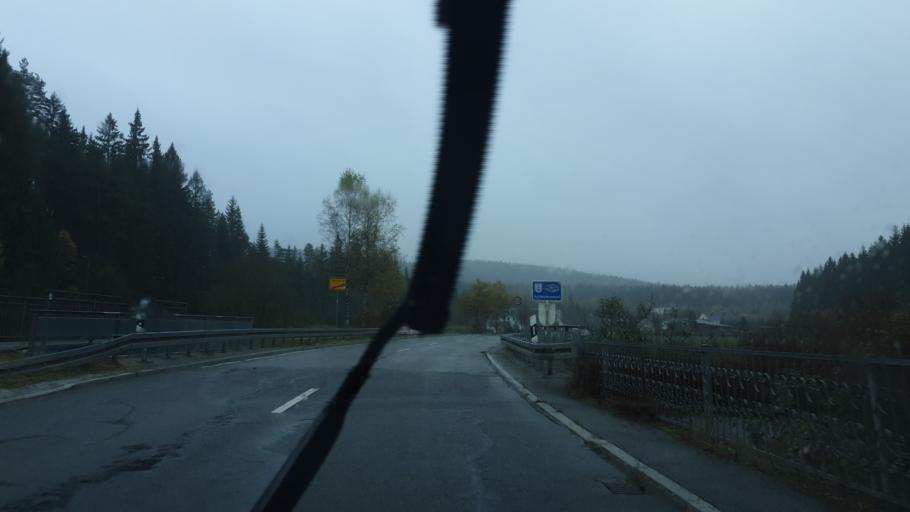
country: DE
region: Saxony
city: Muldenhammer
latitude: 50.4532
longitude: 12.4799
